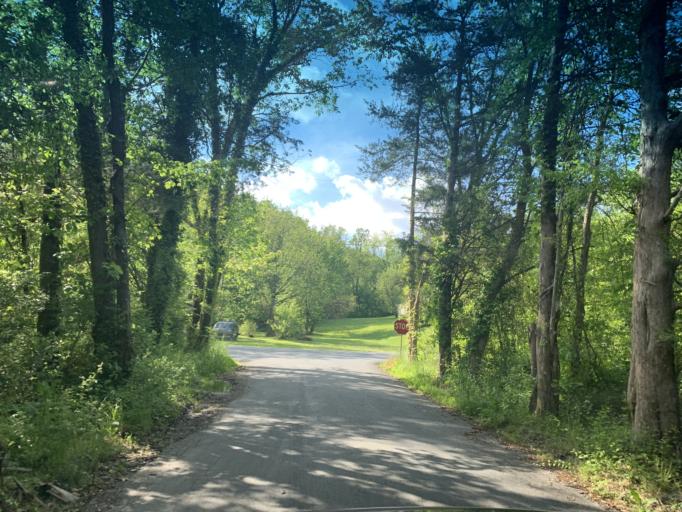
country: US
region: Maryland
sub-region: Cecil County
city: Rising Sun
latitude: 39.6907
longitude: -76.1474
